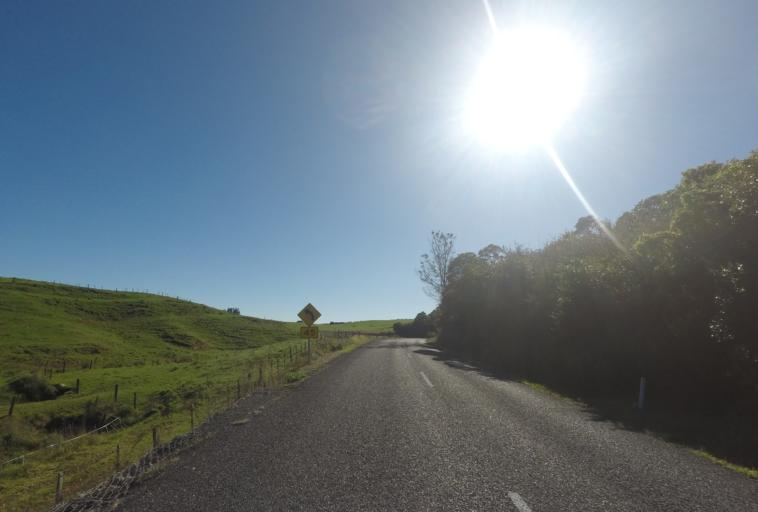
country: NZ
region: Bay of Plenty
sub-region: Western Bay of Plenty District
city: Waihi Beach
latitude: -37.3896
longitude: 175.9053
